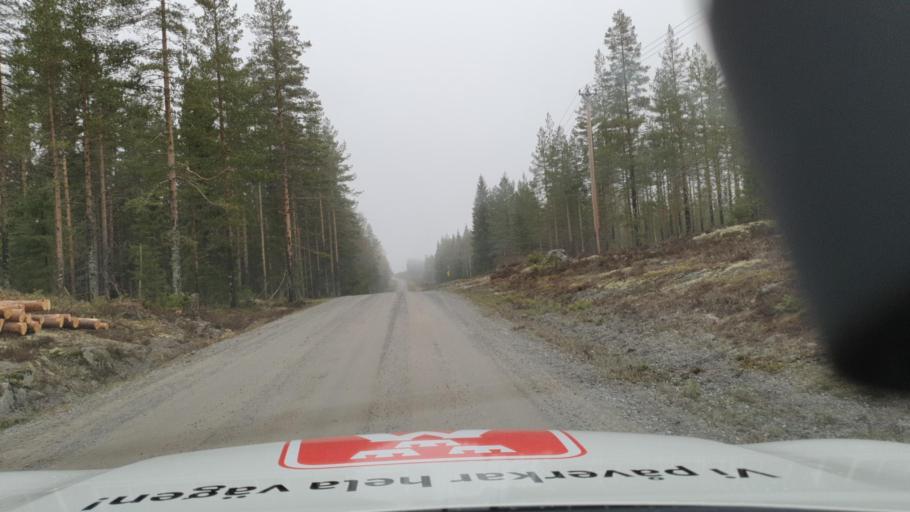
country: SE
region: Vaesterbotten
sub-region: Nordmalings Kommun
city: Nordmaling
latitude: 63.7443
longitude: 19.5013
